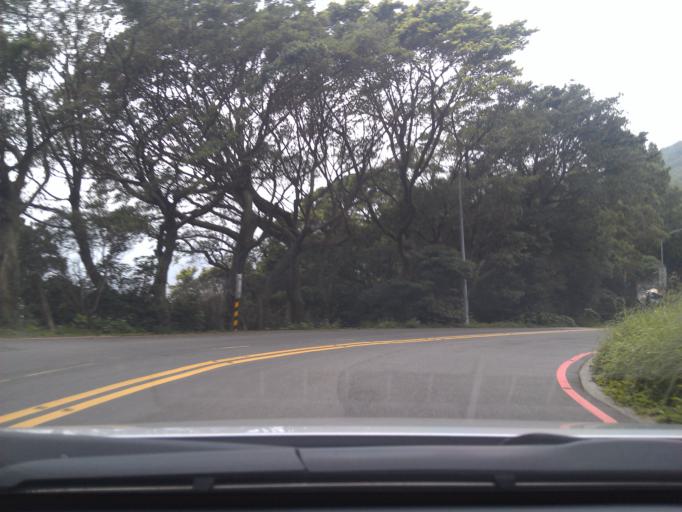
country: TW
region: Taipei
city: Taipei
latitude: 25.1633
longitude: 121.5445
